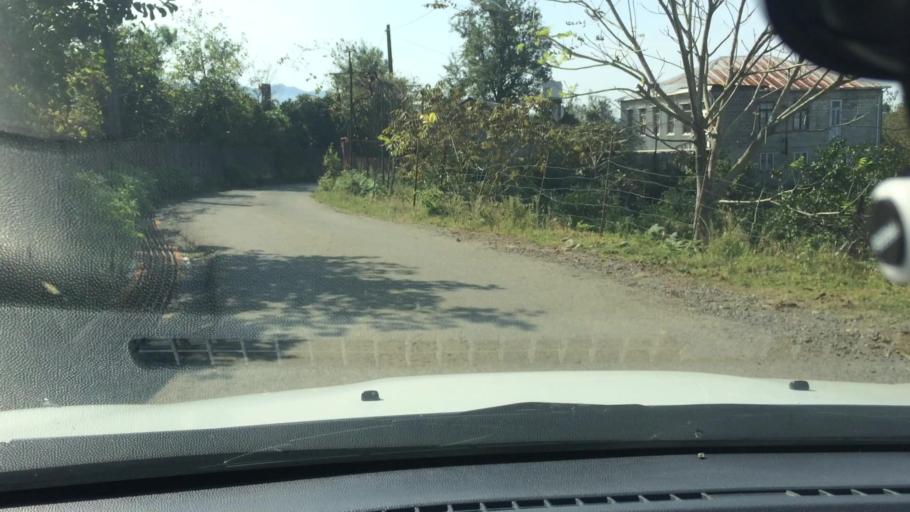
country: GE
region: Ajaria
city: Kobuleti
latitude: 41.8123
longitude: 41.8246
